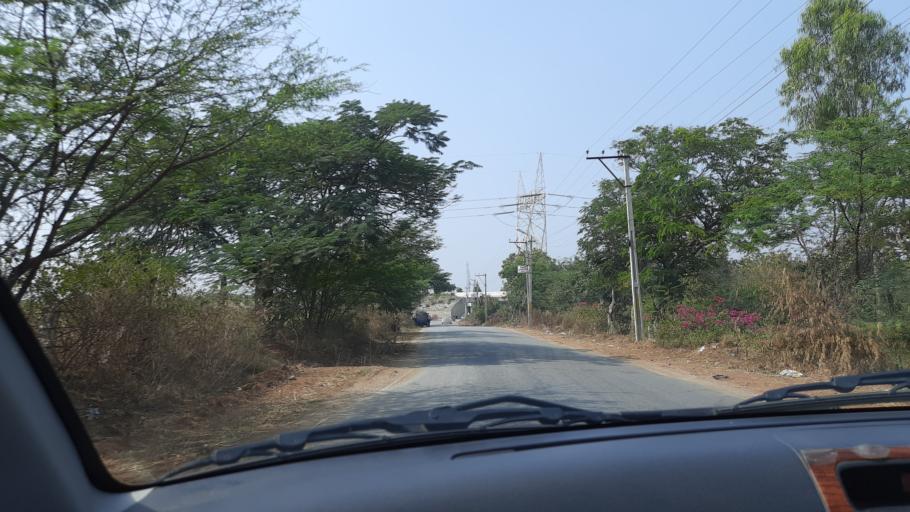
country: IN
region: Telangana
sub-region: Rangareddi
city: Lal Bahadur Nagar
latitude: 17.2805
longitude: 78.6500
